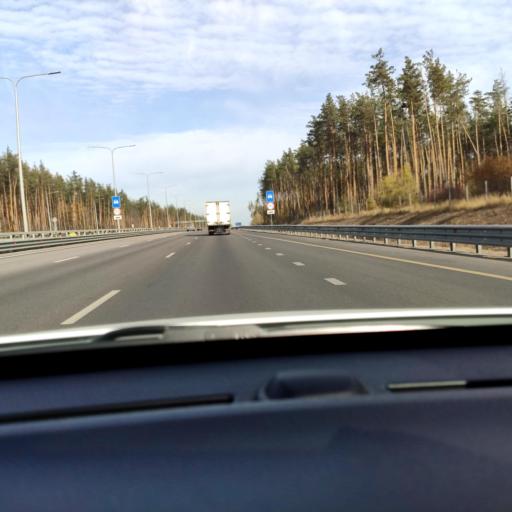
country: RU
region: Voronezj
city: Somovo
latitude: 51.6935
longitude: 39.3036
